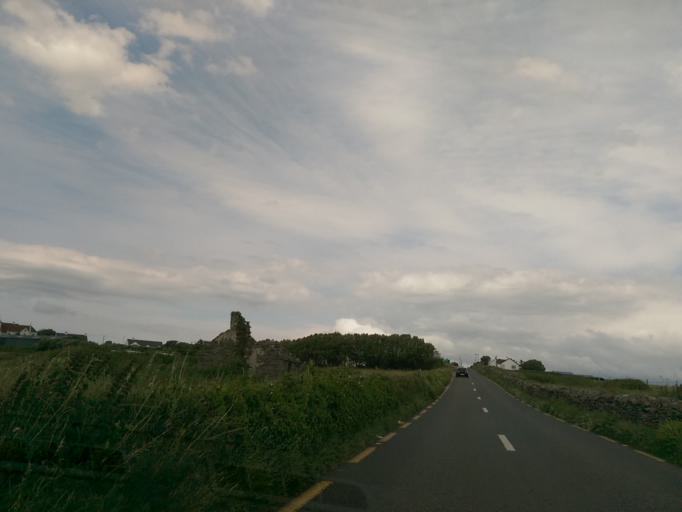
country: IE
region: Munster
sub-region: An Clar
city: Kilrush
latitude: 52.8443
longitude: -9.4217
